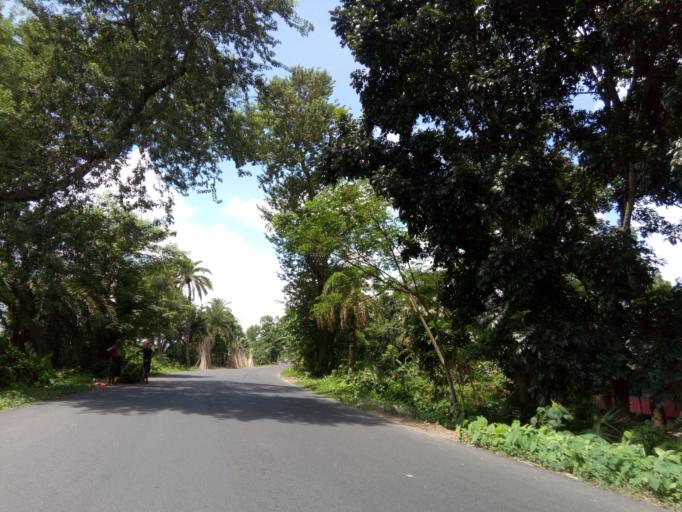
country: BD
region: Dhaka
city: Tungipara
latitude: 22.9104
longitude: 89.8681
